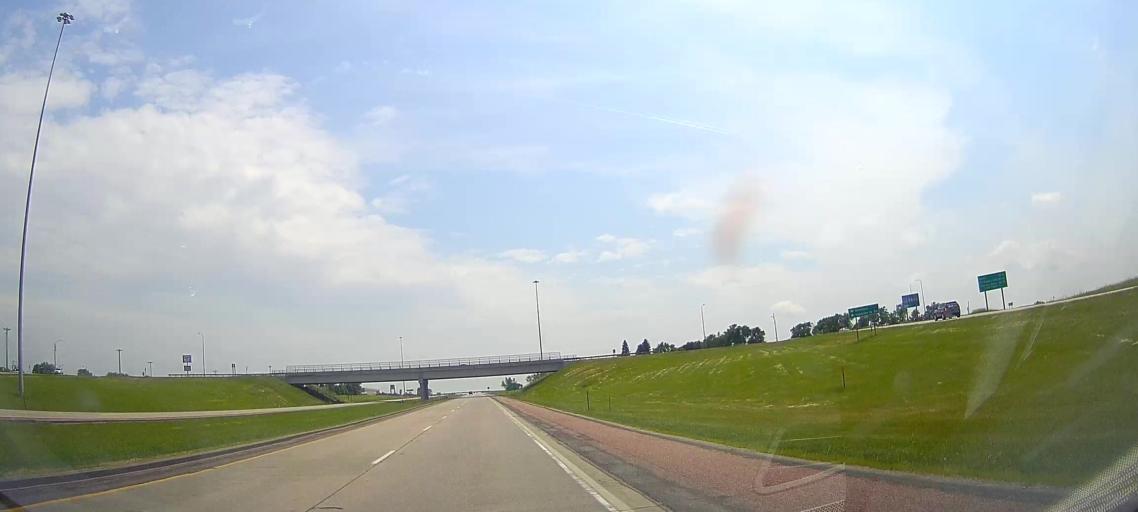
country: US
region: South Dakota
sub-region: Union County
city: Beresford
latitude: 43.0850
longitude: -96.7963
